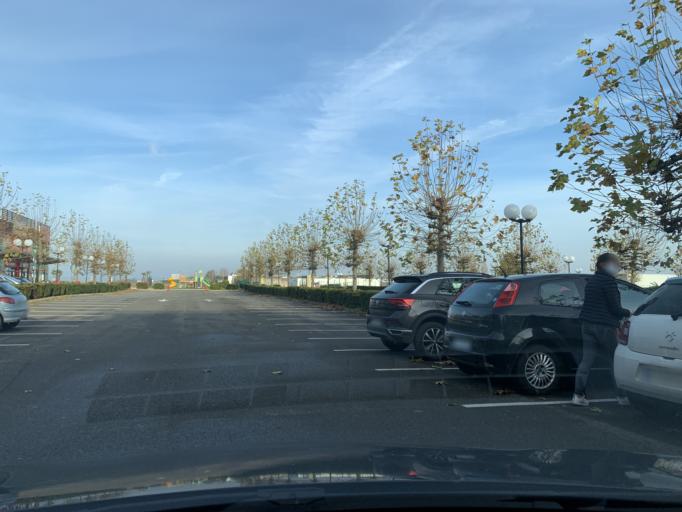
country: FR
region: Nord-Pas-de-Calais
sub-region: Departement du Nord
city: Proville
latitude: 50.1480
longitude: 3.2131
